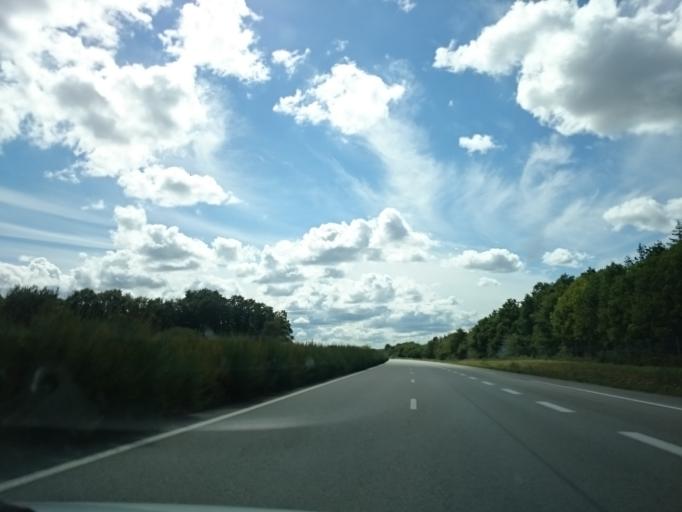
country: FR
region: Pays de la Loire
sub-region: Departement de la Loire-Atlantique
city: Saint-Mars-du-Desert
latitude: 47.3371
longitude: -1.3885
